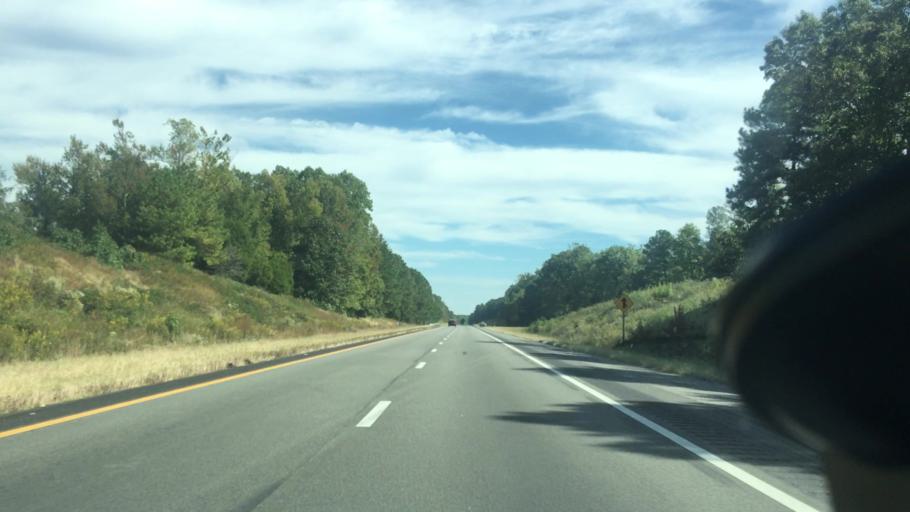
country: US
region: Virginia
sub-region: Chesterfield County
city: Chesterfield
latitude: 37.4085
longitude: -77.5642
